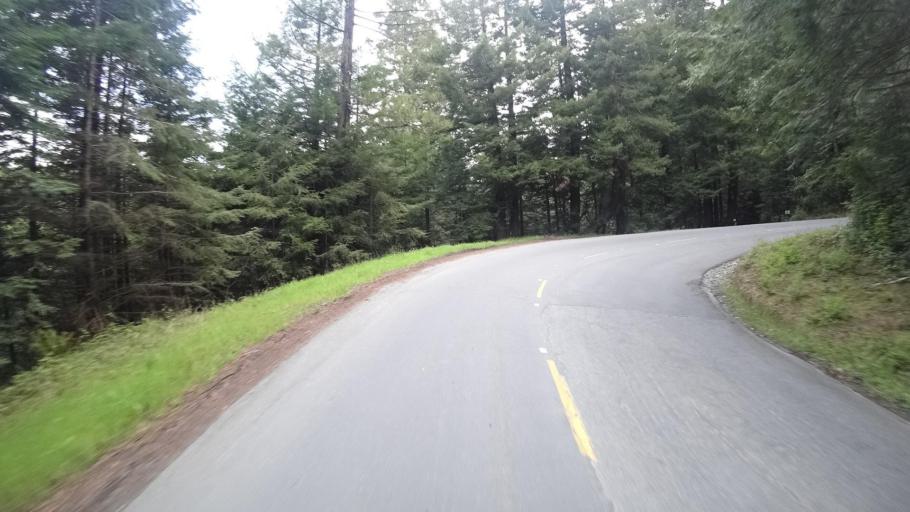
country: US
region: California
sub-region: Humboldt County
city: Bayside
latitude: 40.7574
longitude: -124.0475
